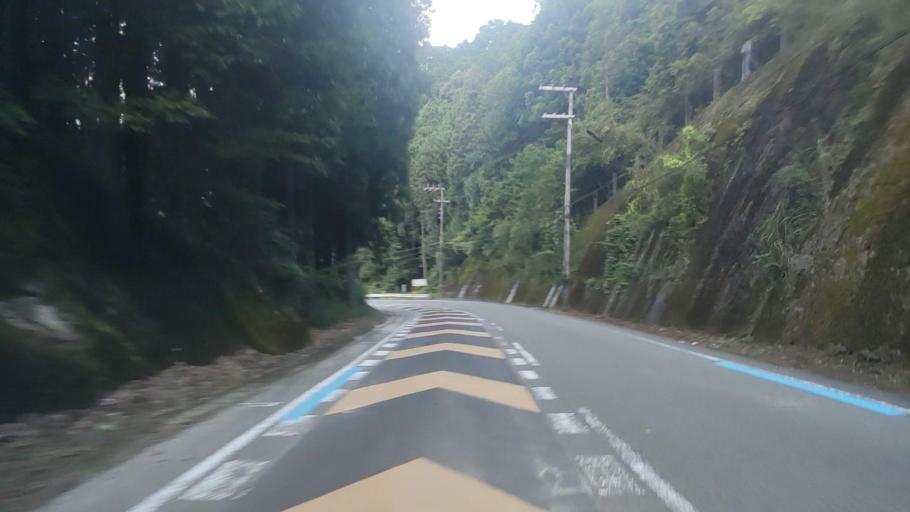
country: JP
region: Wakayama
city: Shingu
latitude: 33.8066
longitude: 135.7278
